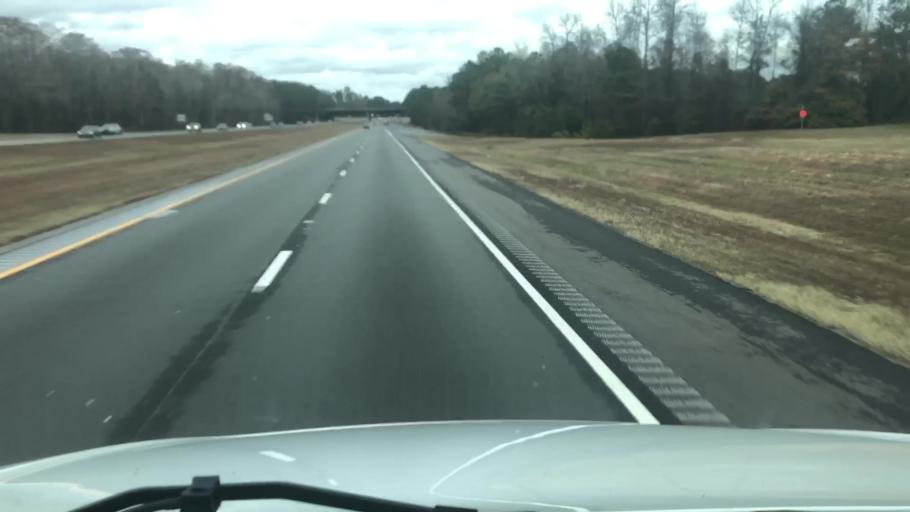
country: US
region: North Carolina
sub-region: Cumberland County
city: Eastover
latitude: 35.0837
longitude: -78.7859
